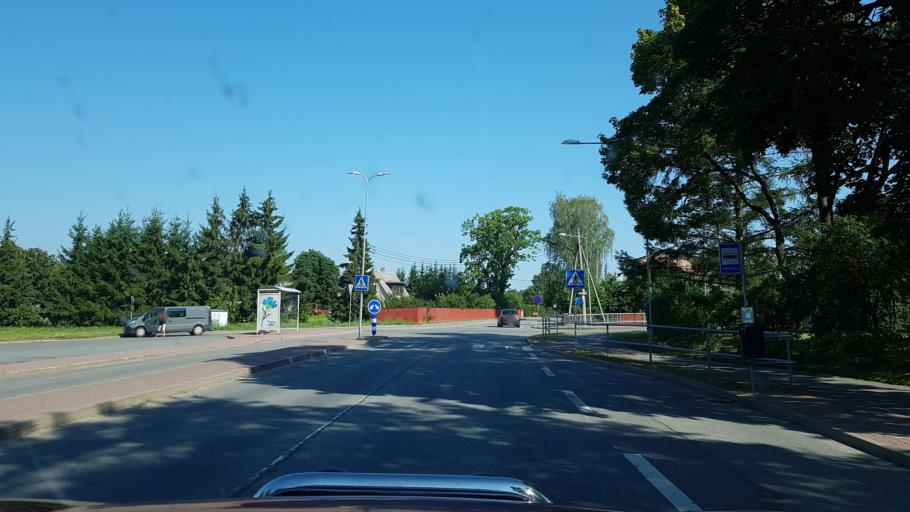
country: EE
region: Tartu
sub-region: Tartu linn
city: Tartu
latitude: 58.4195
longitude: 26.7626
